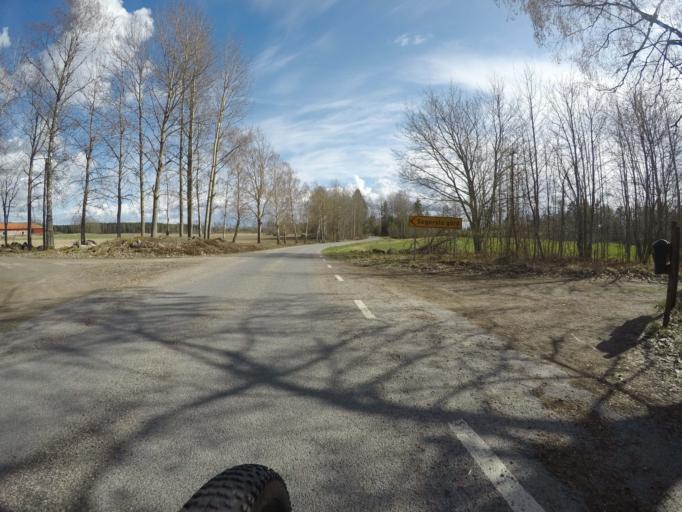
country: SE
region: Vaestmanland
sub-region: Kungsors Kommun
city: Kungsoer
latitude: 59.3091
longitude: 16.1239
